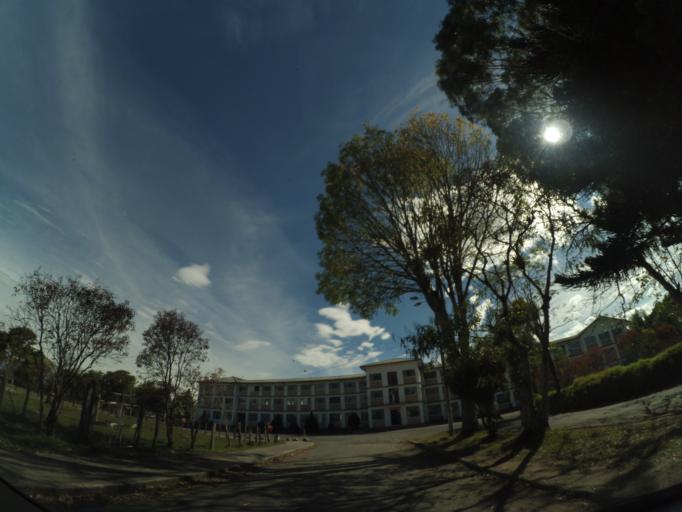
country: CO
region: Cauca
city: Popayan
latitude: 2.4627
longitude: -76.5921
